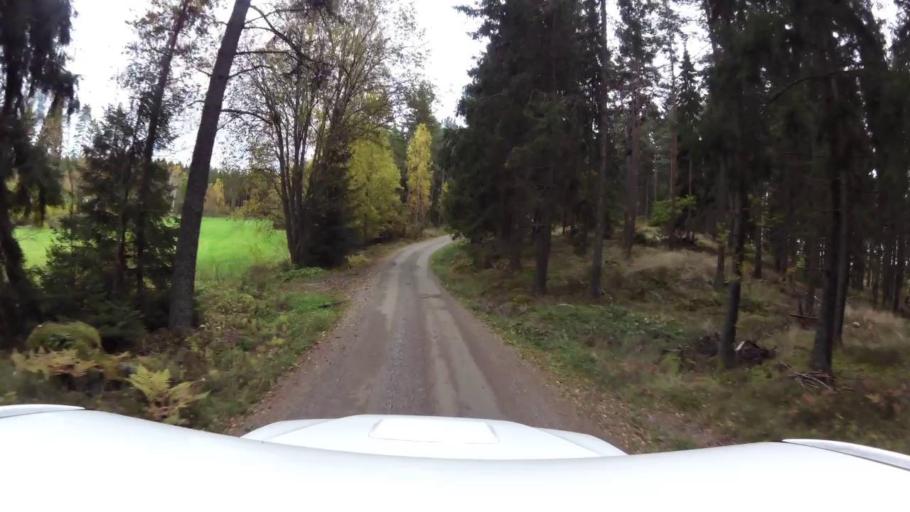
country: SE
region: OEstergoetland
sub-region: Linkopings Kommun
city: Ljungsbro
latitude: 58.5478
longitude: 15.4300
